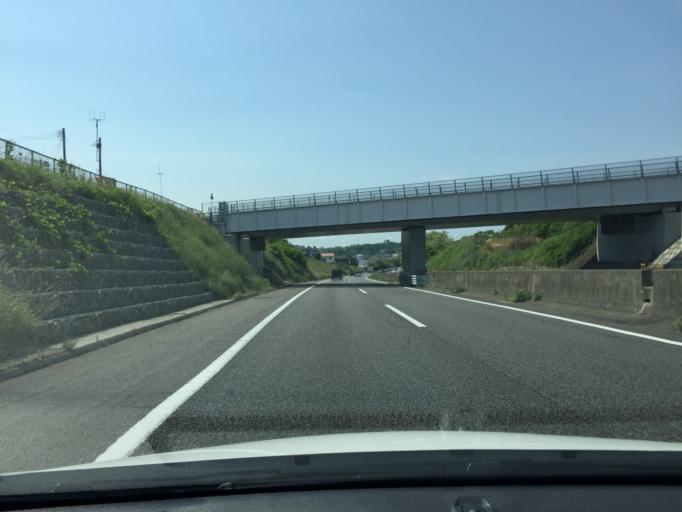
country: JP
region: Fukushima
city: Sukagawa
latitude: 37.3002
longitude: 140.3509
